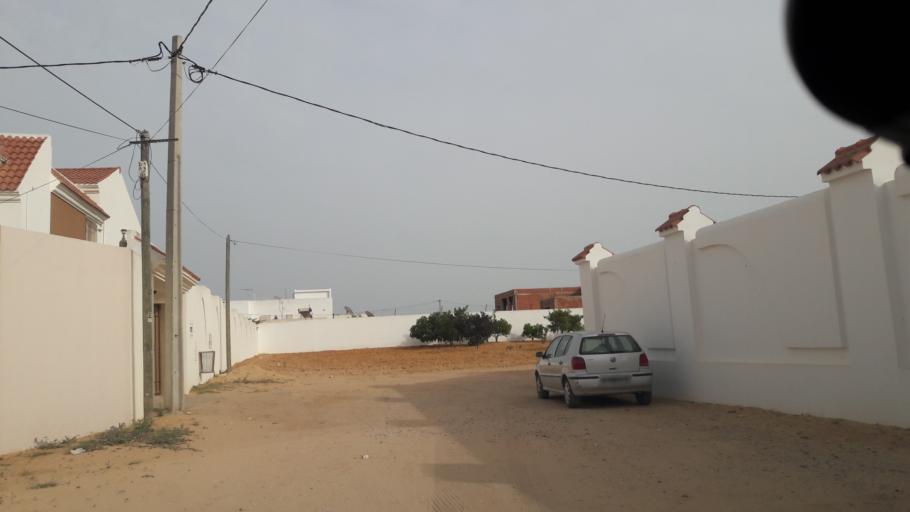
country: TN
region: Safaqis
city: Al Qarmadah
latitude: 34.7790
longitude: 10.7725
